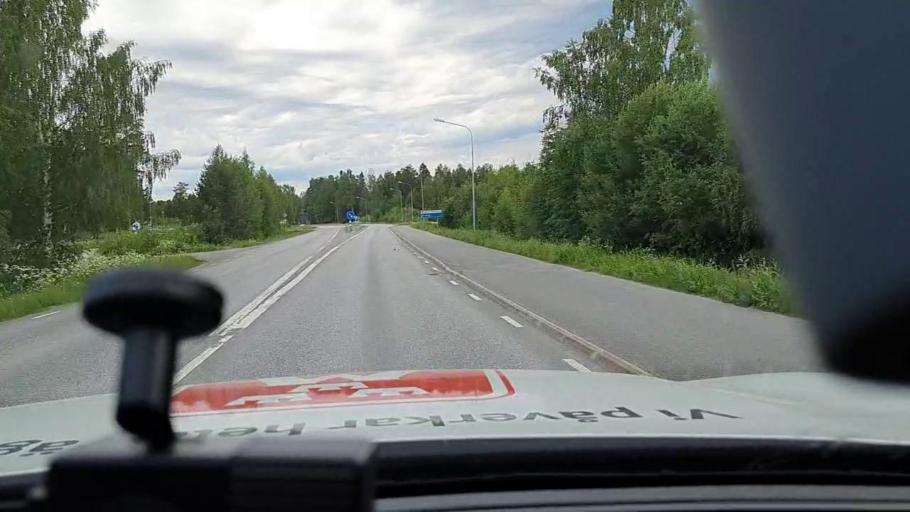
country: SE
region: Norrbotten
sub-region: Bodens Kommun
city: Boden
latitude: 65.8130
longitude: 21.6497
